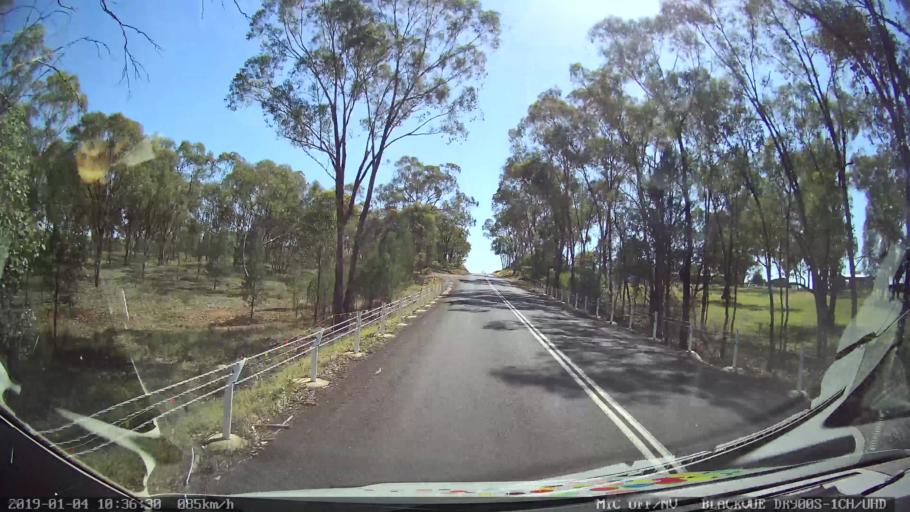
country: AU
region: New South Wales
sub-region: Cabonne
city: Canowindra
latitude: -33.3031
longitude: 148.6850
